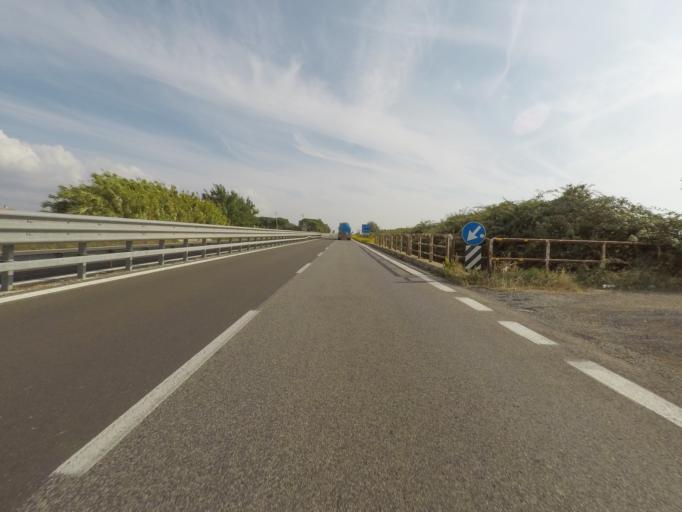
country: IT
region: Latium
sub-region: Provincia di Viterbo
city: Montalto di Castro
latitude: 42.3316
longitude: 11.6280
